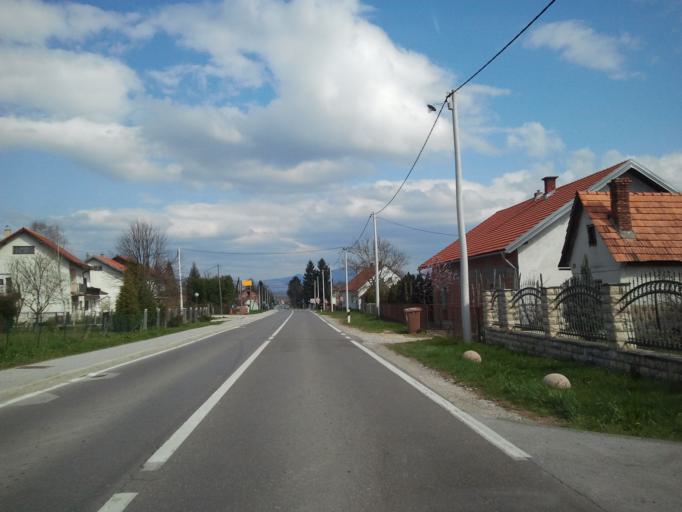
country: HR
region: Zagrebacka
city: Jastrebarsko
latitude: 45.6008
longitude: 15.5986
